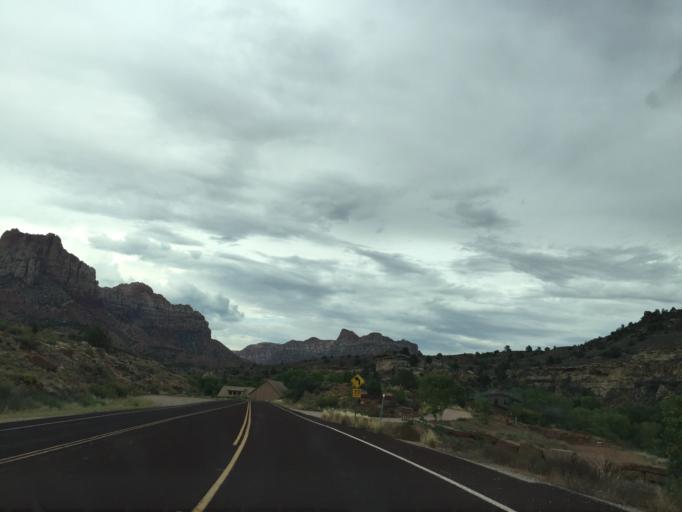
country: US
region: Utah
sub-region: Washington County
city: Hildale
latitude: 37.1607
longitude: -113.0206
